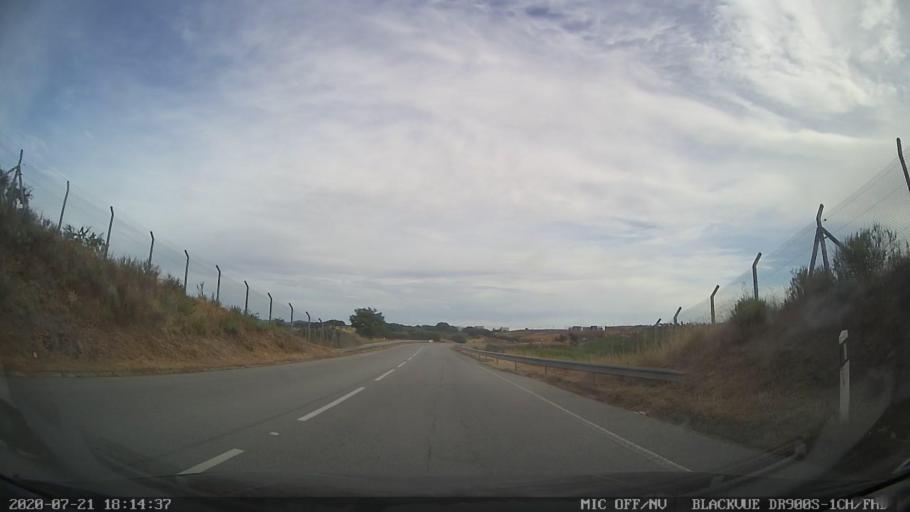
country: PT
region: Viseu
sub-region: Sao Joao da Pesqueira
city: Sao Joao da Pesqueira
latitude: 41.1235
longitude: -7.3907
